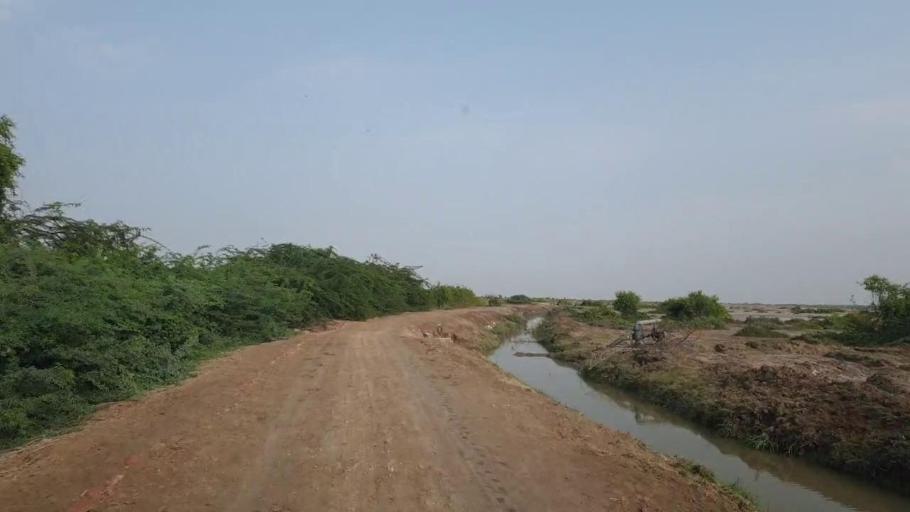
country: PK
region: Sindh
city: Kadhan
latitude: 24.4445
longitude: 68.8082
